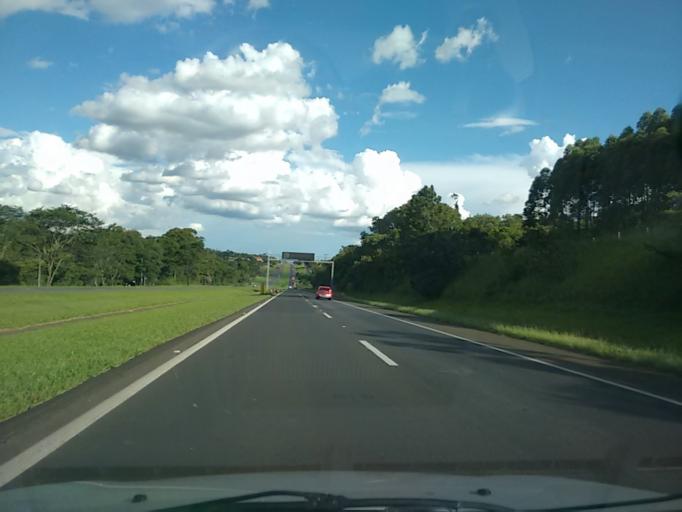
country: BR
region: Sao Paulo
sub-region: Sao Carlos
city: Sao Carlos
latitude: -22.0619
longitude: -47.8512
